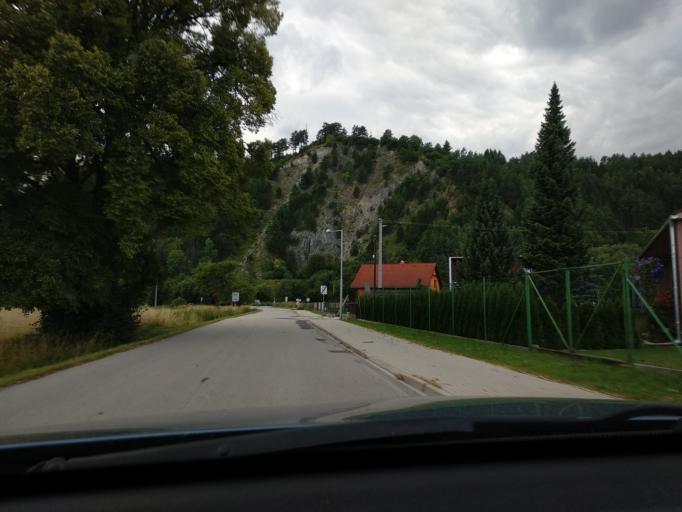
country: SK
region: Zilinsky
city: Ruzomberok
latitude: 49.0868
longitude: 19.3429
